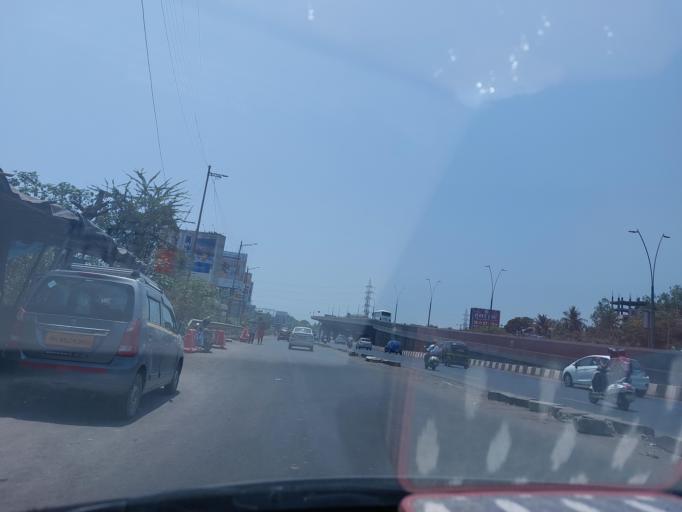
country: IN
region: Maharashtra
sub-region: Mumbai Suburban
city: Mumbai
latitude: 19.0503
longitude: 72.8743
